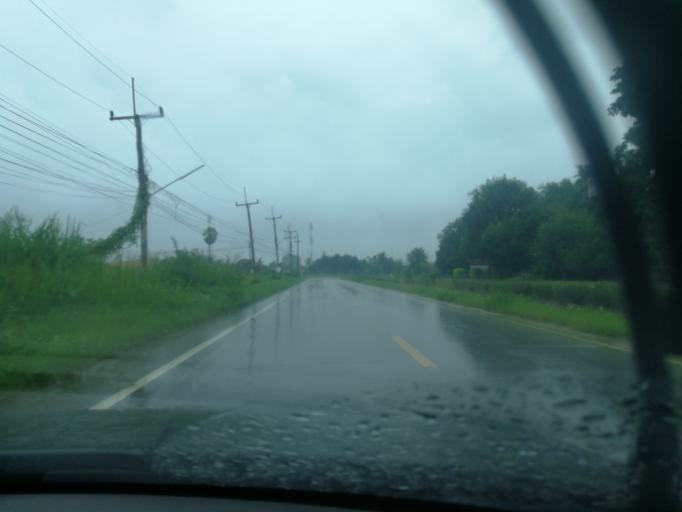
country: TH
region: Chiang Mai
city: San Pa Tong
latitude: 18.6254
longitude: 98.8986
